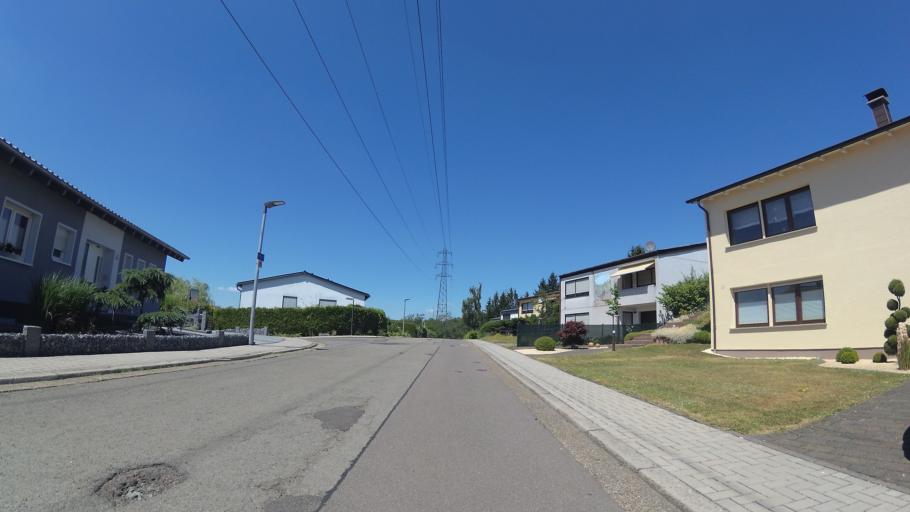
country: DE
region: Saarland
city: Hangard
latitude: 49.3772
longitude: 7.1910
